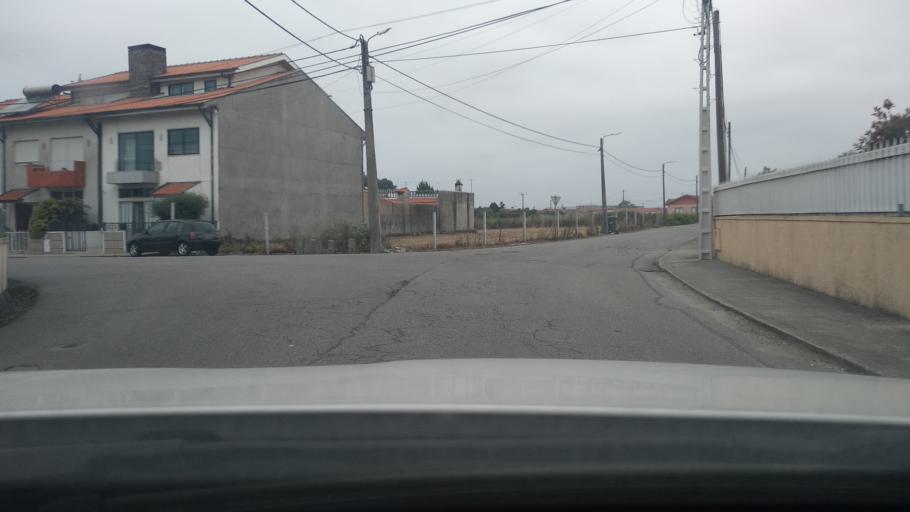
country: PT
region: Aveiro
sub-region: Espinho
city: Silvalde
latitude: 40.9901
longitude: -8.6363
